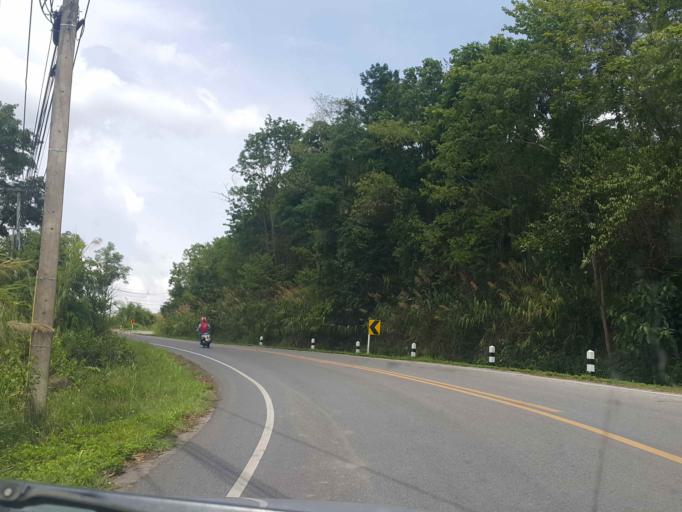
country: TH
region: Nan
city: Ban Luang
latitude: 18.8618
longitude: 100.4607
